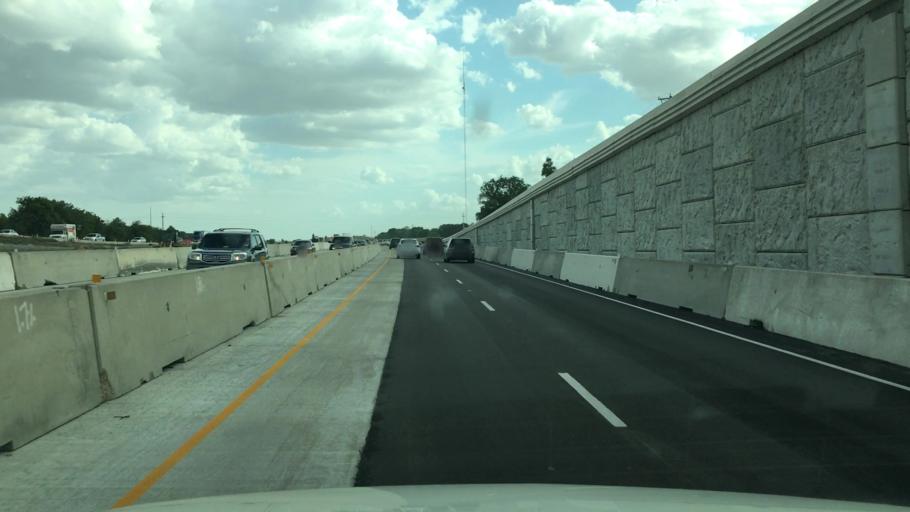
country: US
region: Texas
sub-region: McLennan County
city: Bruceville-Eddy
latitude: 31.2944
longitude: -97.2531
